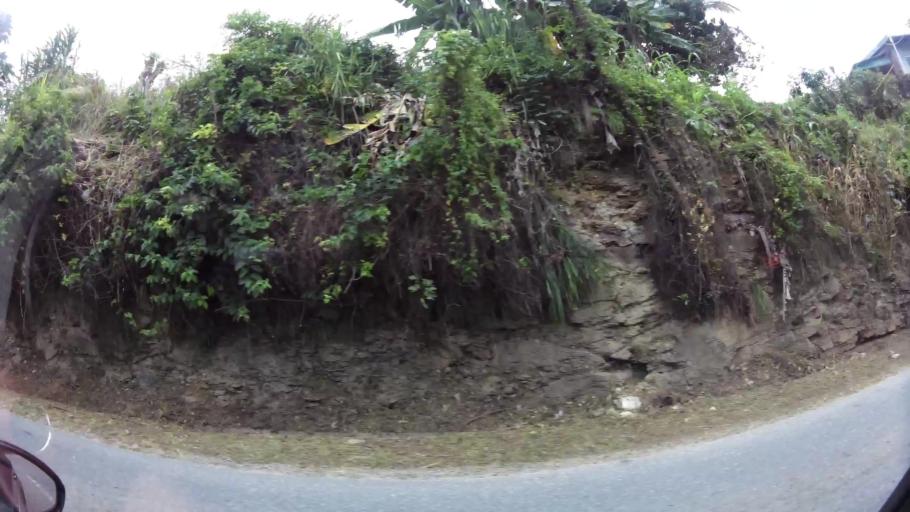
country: TT
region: Diego Martin
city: Petit Valley
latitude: 10.7205
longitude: -61.4968
